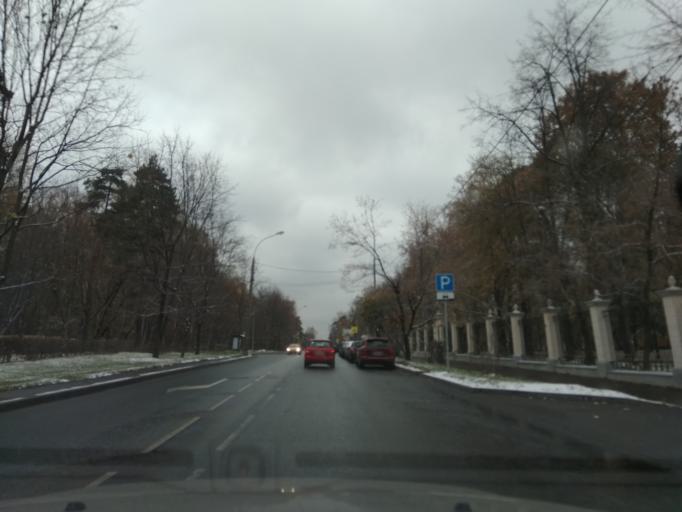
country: RU
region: Moscow
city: Pokrovskoye-Streshnevo
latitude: 55.8036
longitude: 37.4768
